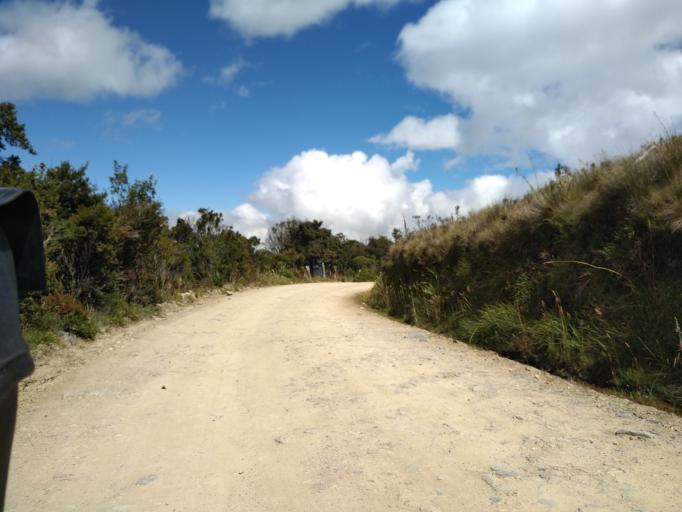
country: CO
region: Boyaca
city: Duitama
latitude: 5.9326
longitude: -73.0911
